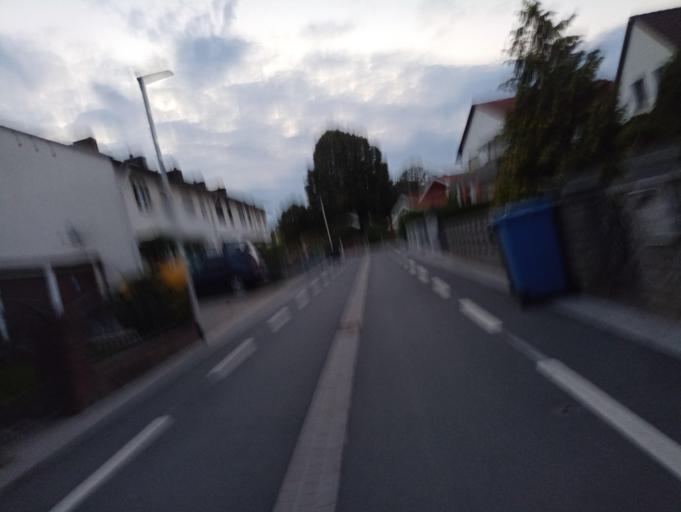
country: DE
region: Hesse
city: Langen
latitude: 49.9825
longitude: 8.6565
